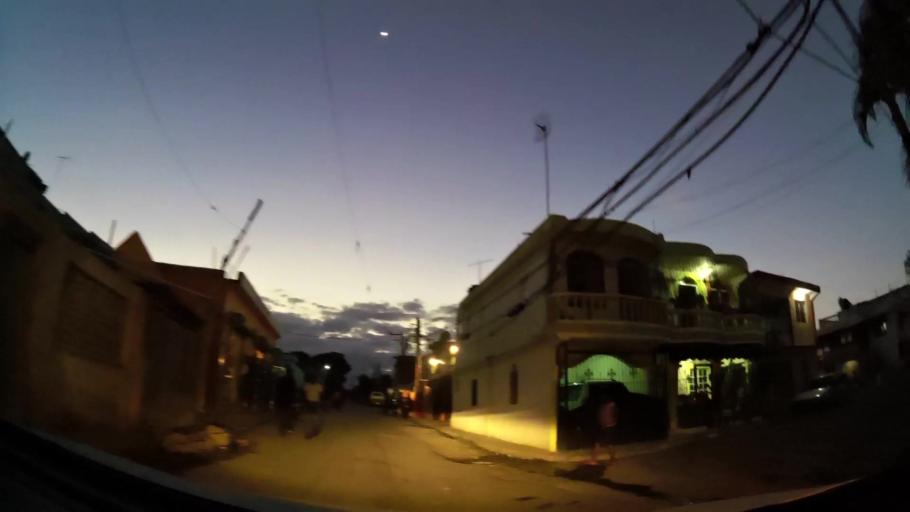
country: DO
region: Nacional
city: La Agustina
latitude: 18.5398
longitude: -69.9405
